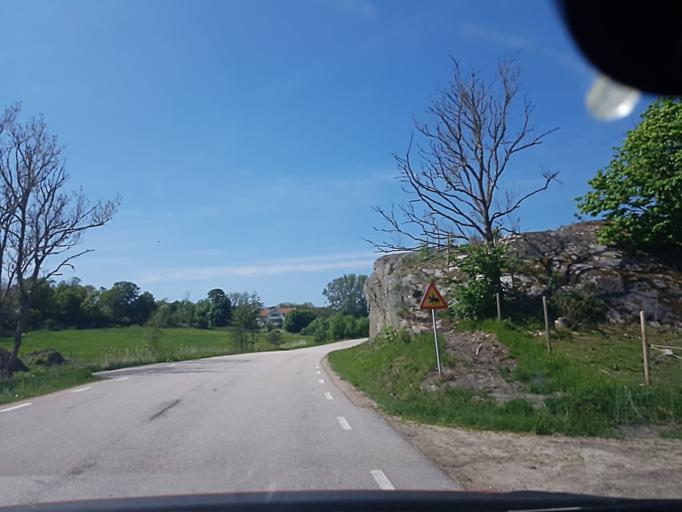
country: SE
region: Vaestra Goetaland
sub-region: Lysekils Kommun
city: Lysekil
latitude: 58.1593
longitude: 11.4584
